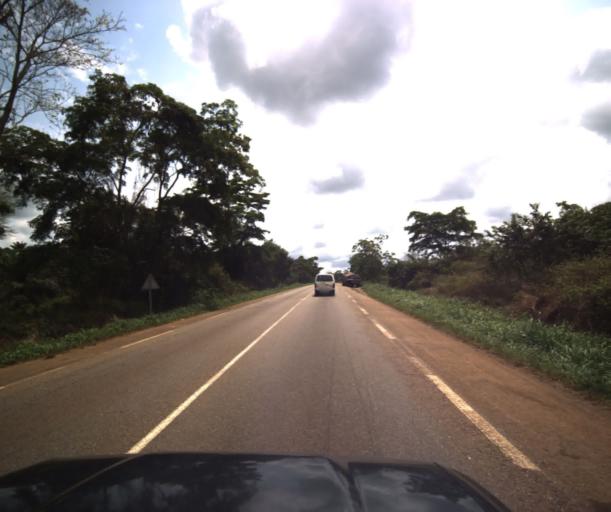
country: CM
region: Centre
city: Eseka
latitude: 3.8602
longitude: 10.5849
